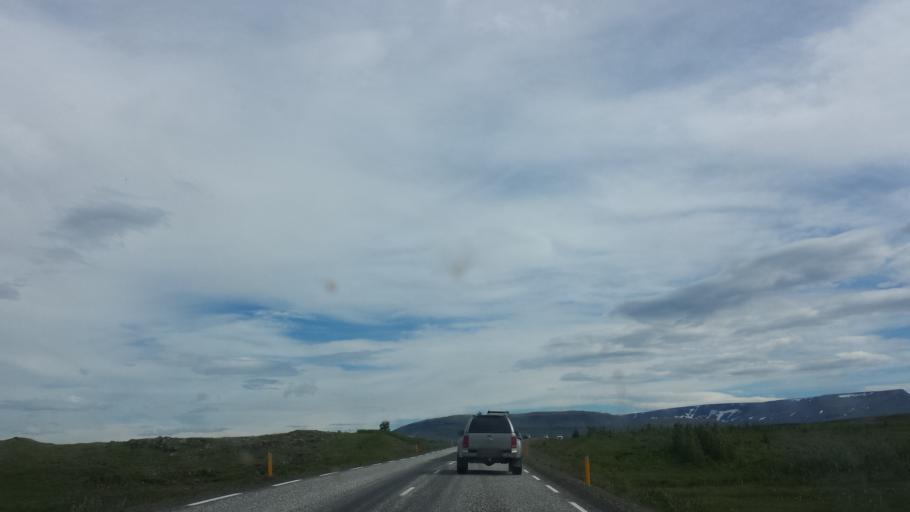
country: IS
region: West
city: Borgarnes
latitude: 64.3727
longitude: -21.8390
